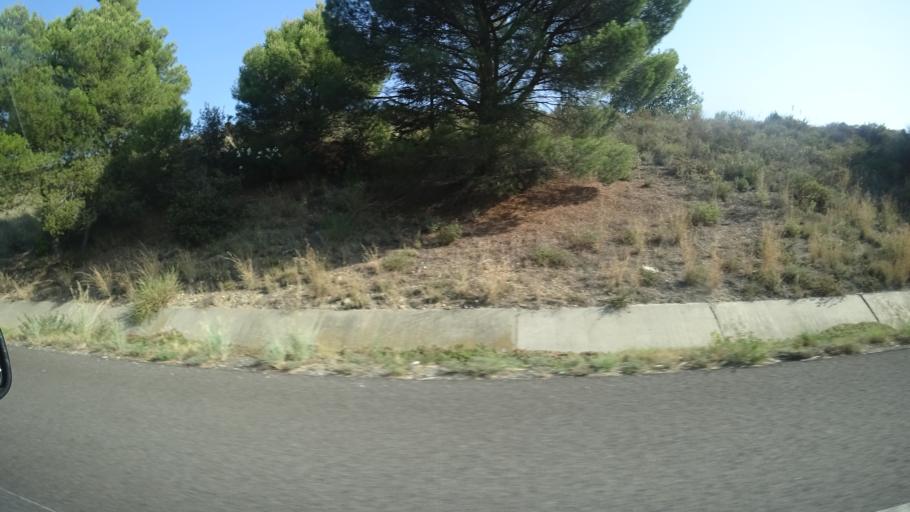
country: FR
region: Languedoc-Roussillon
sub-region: Departement des Pyrenees-Orientales
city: Vinca
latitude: 42.6510
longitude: 2.5387
